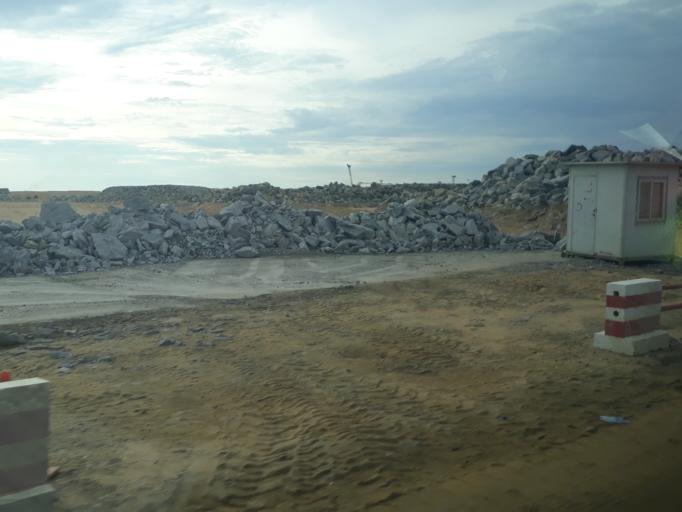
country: LK
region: Western
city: Colombo
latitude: 6.9371
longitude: 79.8373
